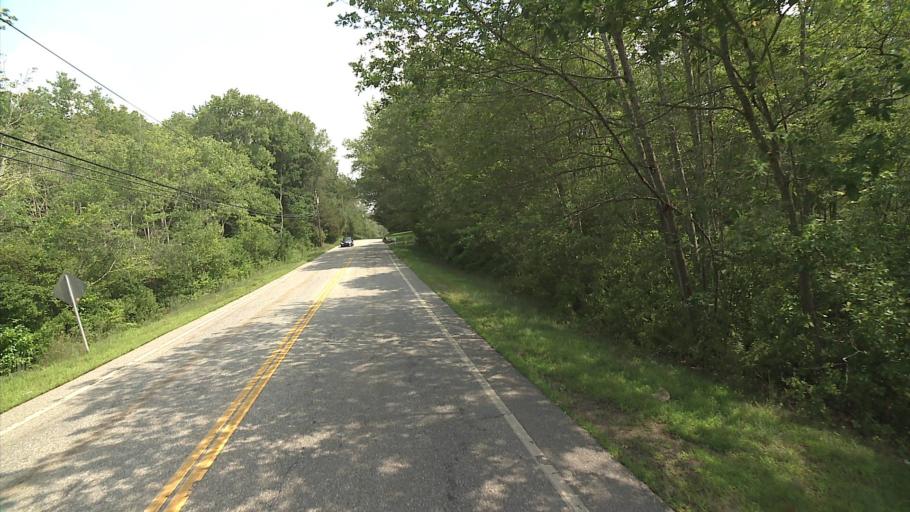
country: US
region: Connecticut
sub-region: Middlesex County
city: Essex Village
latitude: 41.4385
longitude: -72.3375
